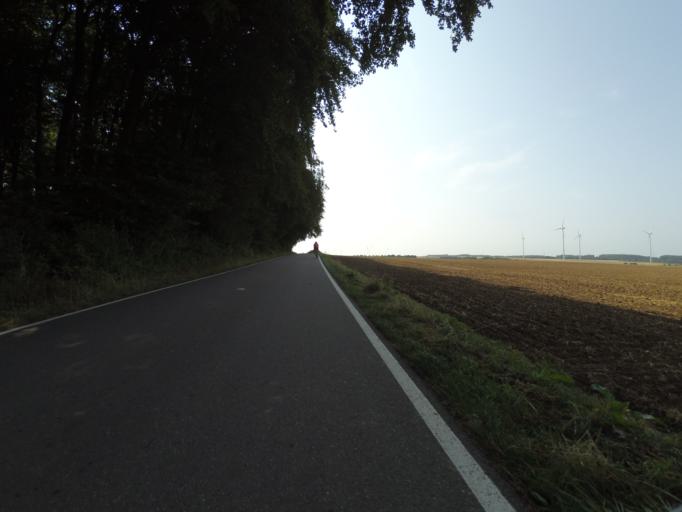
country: DE
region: Saarland
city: Perl
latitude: 49.5057
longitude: 6.4303
